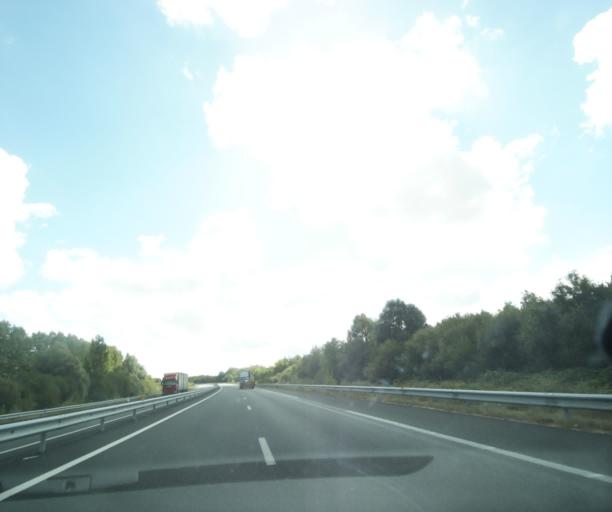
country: FR
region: Poitou-Charentes
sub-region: Departement de la Charente-Maritime
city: Bords
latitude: 45.9136
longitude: -0.8123
